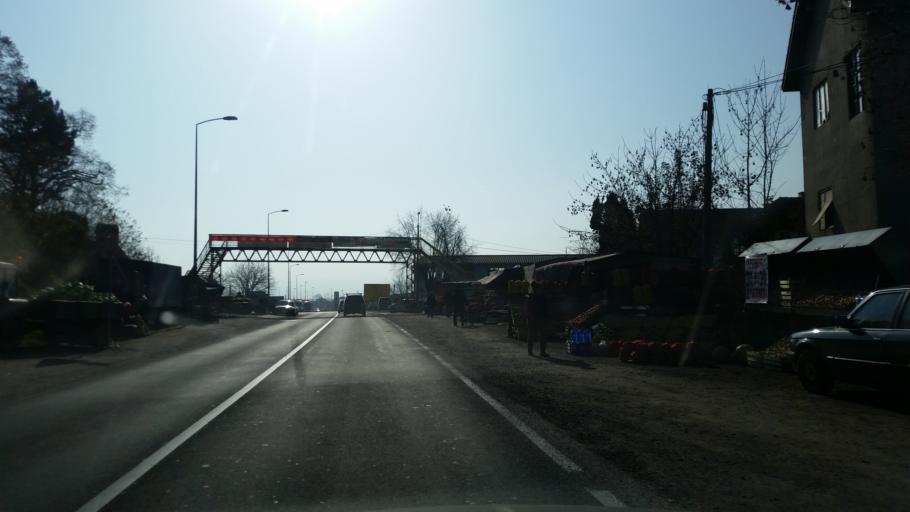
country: RS
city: Prislonica
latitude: 43.9164
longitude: 20.4077
